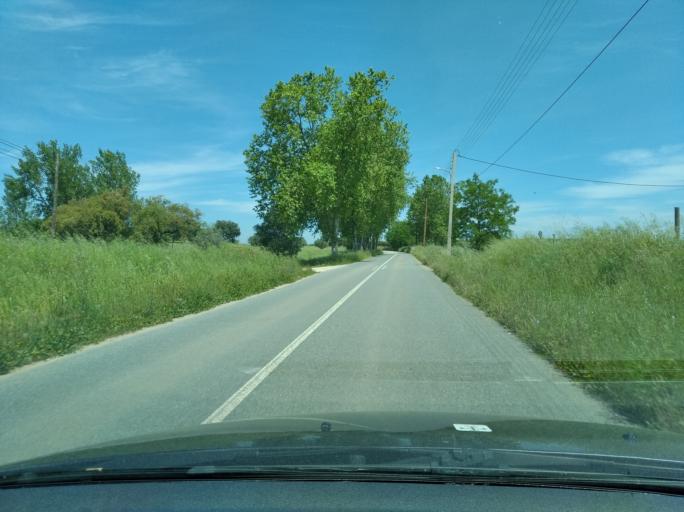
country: PT
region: Portalegre
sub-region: Avis
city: Avis
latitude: 39.0942
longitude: -7.8794
